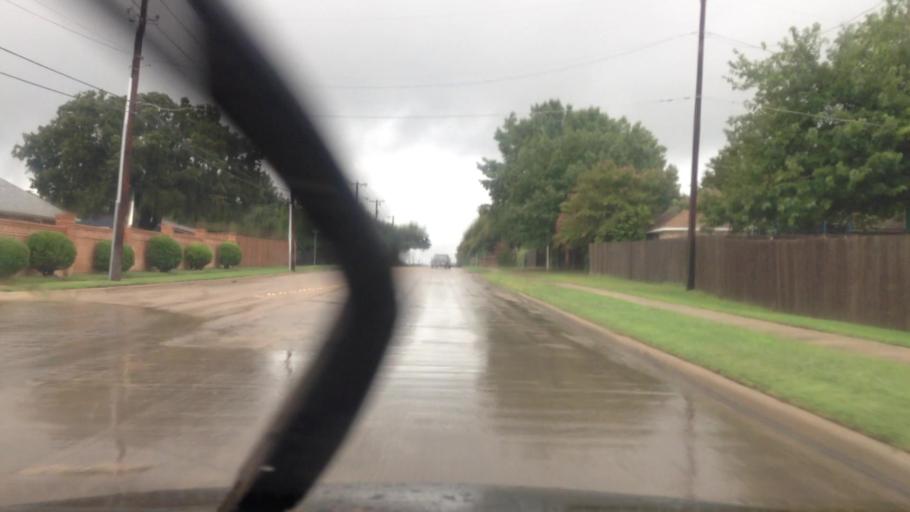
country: US
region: Texas
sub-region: Tarrant County
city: Watauga
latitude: 32.8821
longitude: -97.2177
